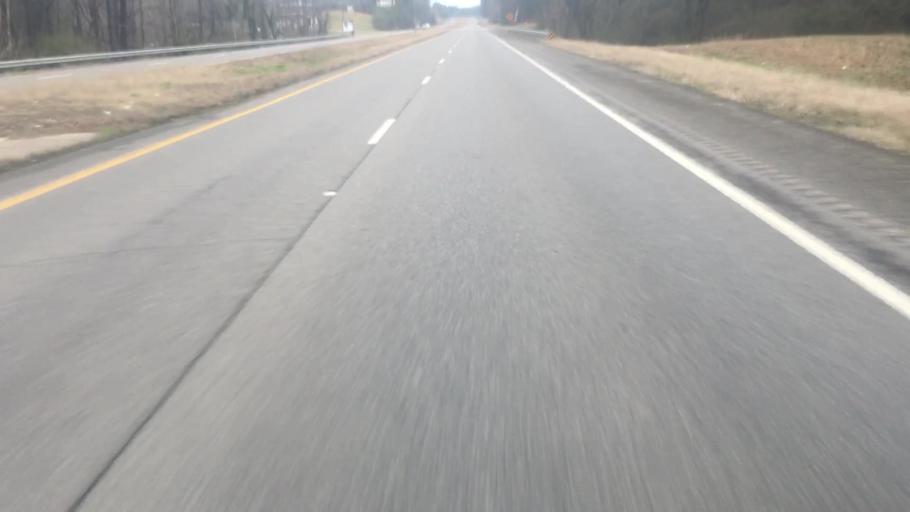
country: US
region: Alabama
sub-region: Walker County
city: Cordova
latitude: 33.8212
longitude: -87.1797
